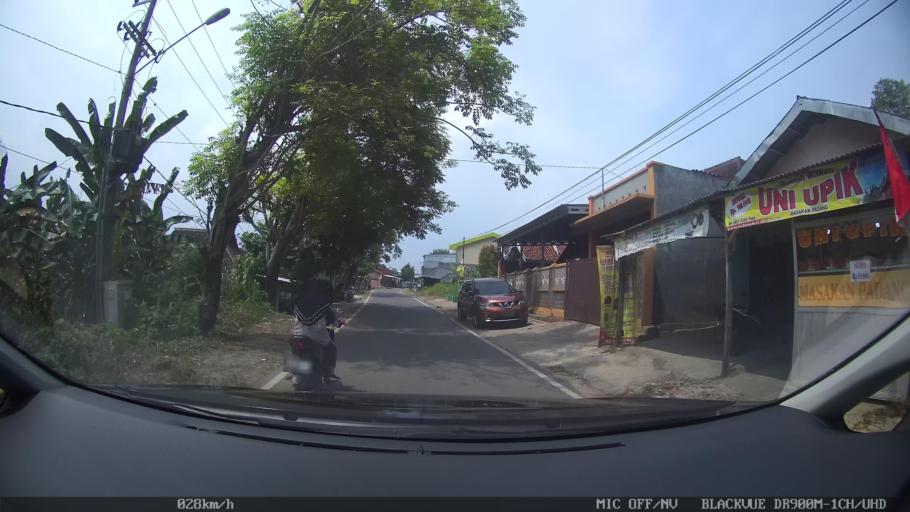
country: ID
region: Lampung
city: Bandarlampung
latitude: -5.4536
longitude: 105.2483
